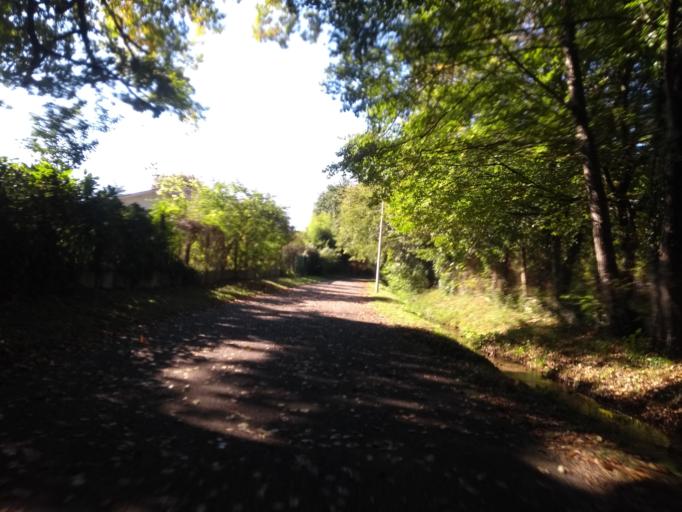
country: FR
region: Aquitaine
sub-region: Departement de la Gironde
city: Pessac
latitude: 44.7958
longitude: -0.6276
